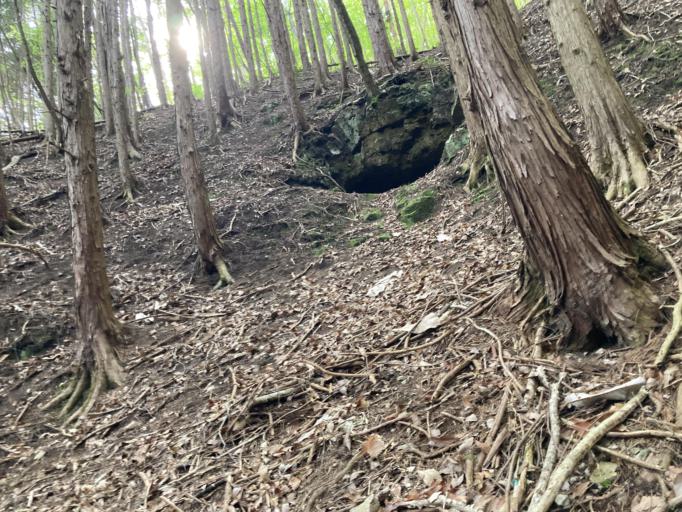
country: JP
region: Fukushima
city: Iwaki
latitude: 37.1630
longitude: 140.8016
